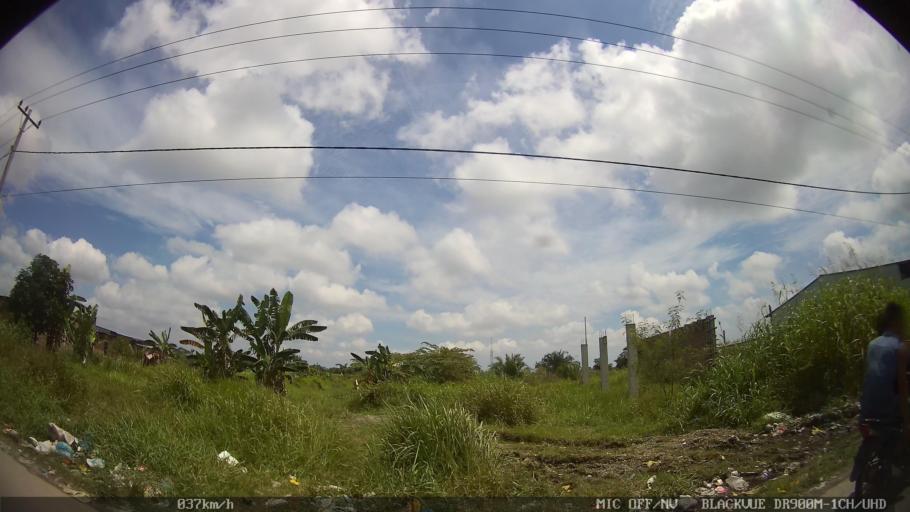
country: ID
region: North Sumatra
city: Percut
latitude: 3.6201
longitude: 98.7726
